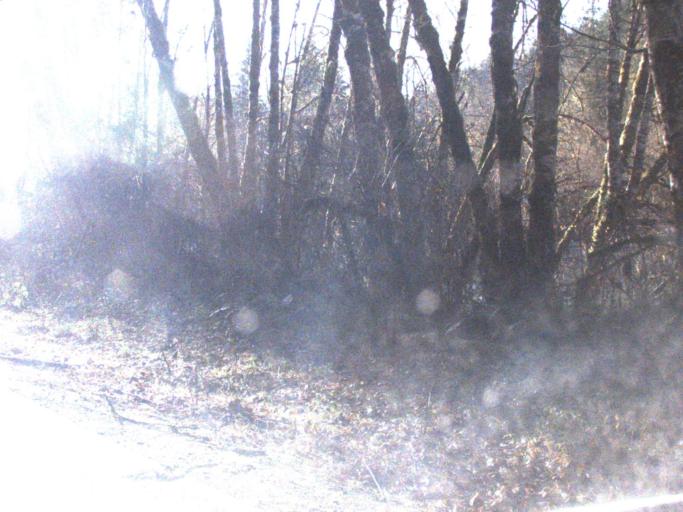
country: US
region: Washington
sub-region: Snohomish County
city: Darrington
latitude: 48.4112
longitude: -121.5559
